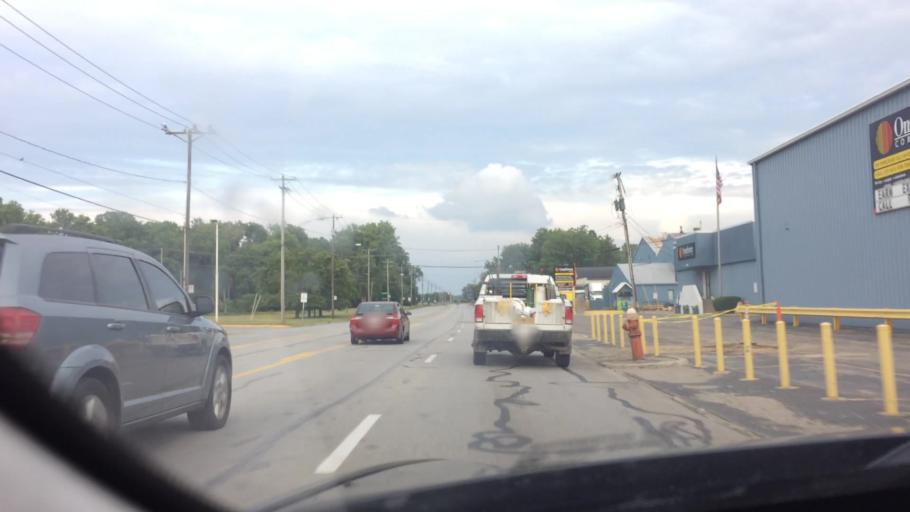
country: US
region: Ohio
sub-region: Lucas County
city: Ottawa Hills
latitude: 41.6380
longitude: -83.6039
